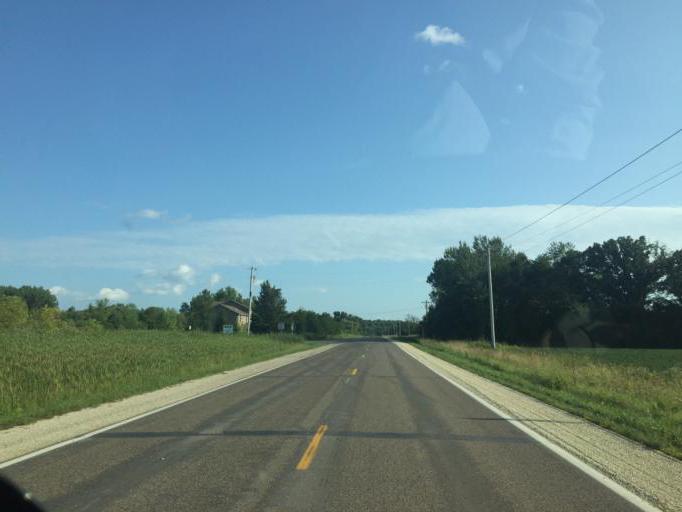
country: US
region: Minnesota
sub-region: Olmsted County
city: Rochester
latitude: 43.9648
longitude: -92.5581
